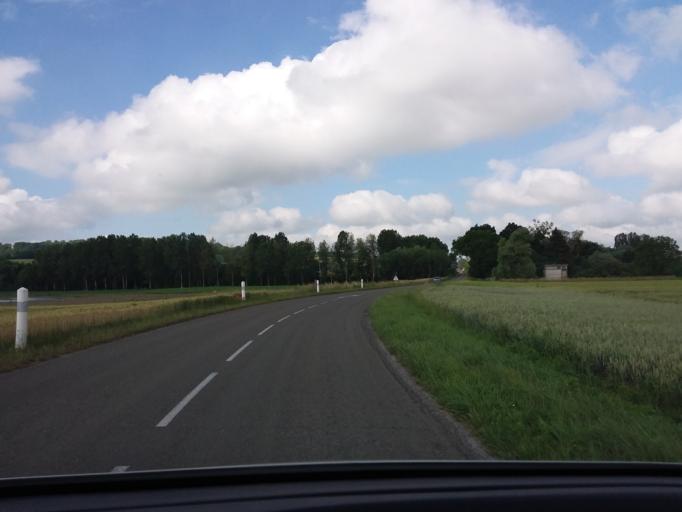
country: FR
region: Champagne-Ardenne
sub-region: Departement de la Marne
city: Fismes
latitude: 49.3830
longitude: 3.7364
